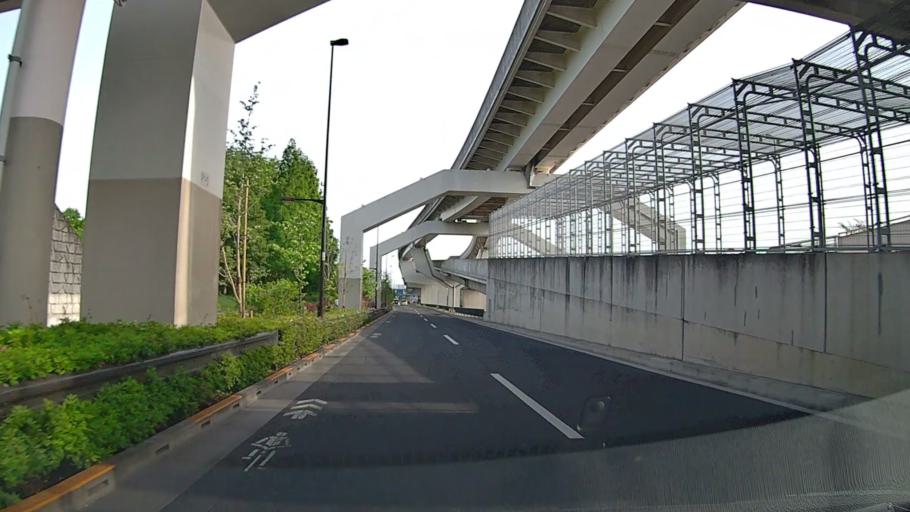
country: JP
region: Saitama
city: Soka
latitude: 35.7999
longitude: 139.7703
